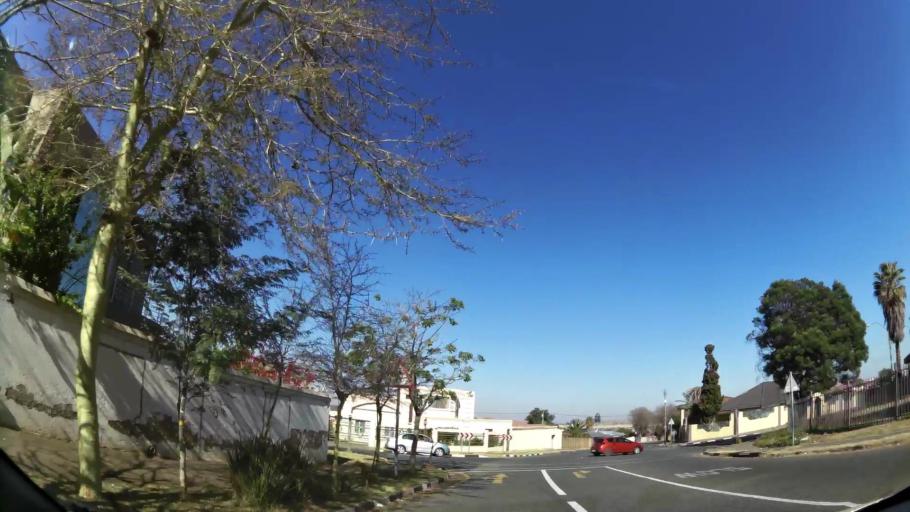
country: ZA
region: Gauteng
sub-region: City of Johannesburg Metropolitan Municipality
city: Johannesburg
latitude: -26.1925
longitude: 27.9904
